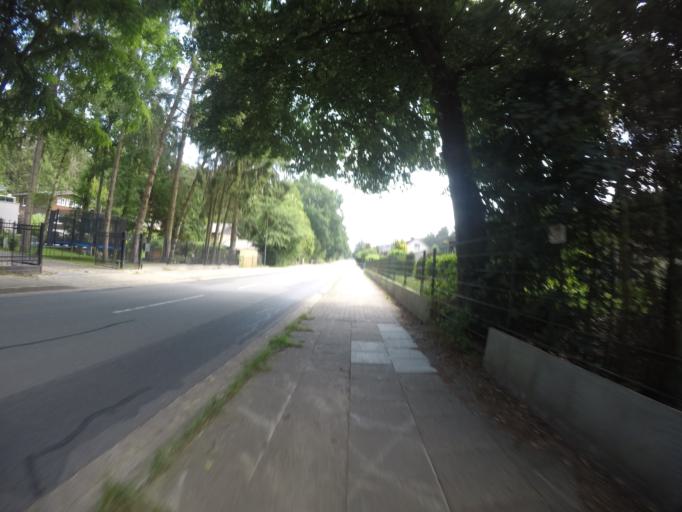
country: DE
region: Lower Saxony
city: Buchholz in der Nordheide
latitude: 53.2868
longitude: 9.8544
